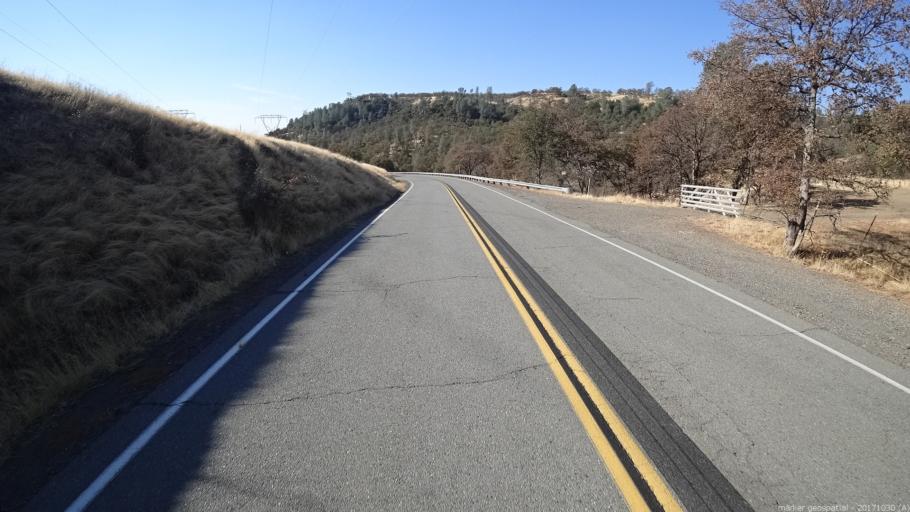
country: US
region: California
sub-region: Shasta County
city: Bella Vista
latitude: 40.6587
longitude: -122.0729
